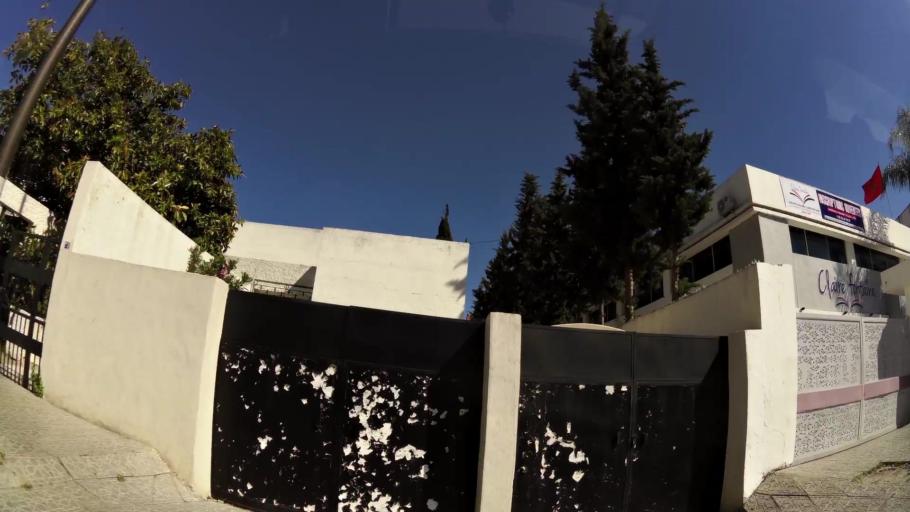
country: MA
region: Fes-Boulemane
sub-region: Fes
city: Fes
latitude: 34.0245
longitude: -4.9966
